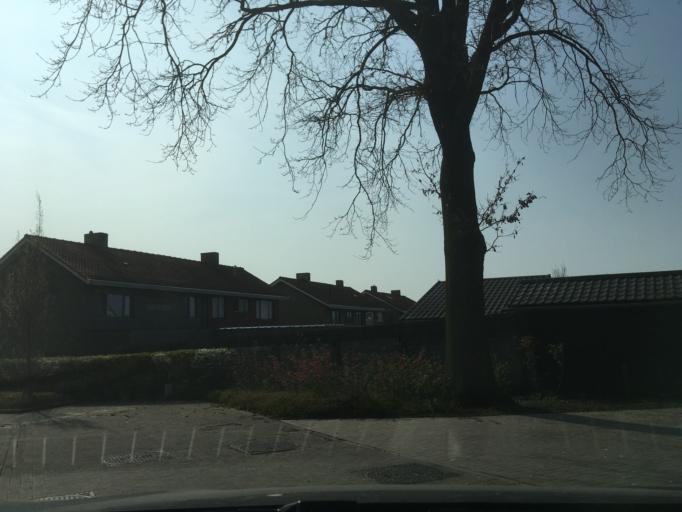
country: BE
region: Flanders
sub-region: Provincie West-Vlaanderen
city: Lichtervelde
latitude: 51.0357
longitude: 3.2069
